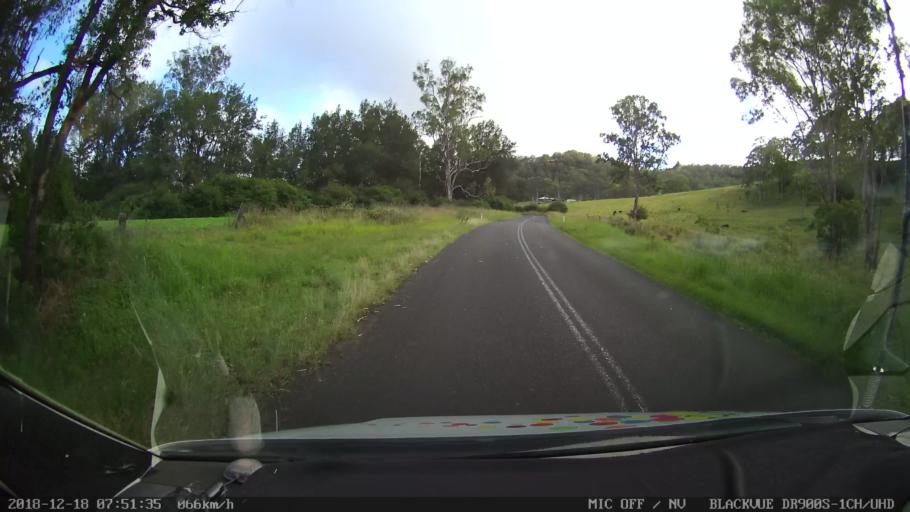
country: AU
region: New South Wales
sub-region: Kyogle
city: Kyogle
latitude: -28.4363
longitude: 152.5796
